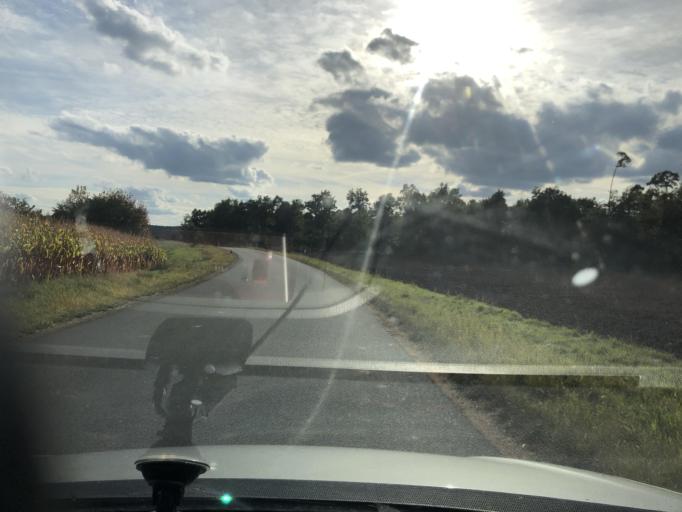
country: DE
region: Bavaria
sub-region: Regierungsbezirk Mittelfranken
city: Cadolzburg
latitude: 49.4797
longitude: 10.8265
